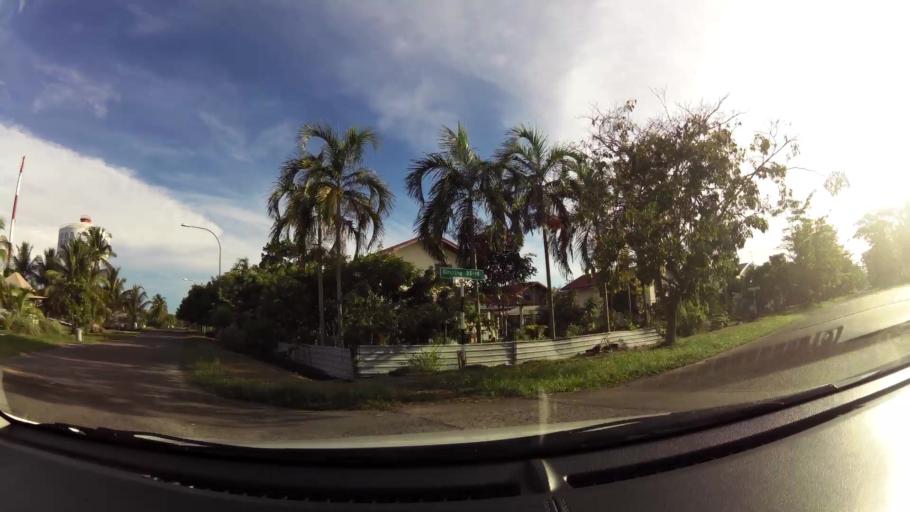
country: BN
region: Belait
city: Kuala Belait
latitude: 4.5770
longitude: 114.2268
